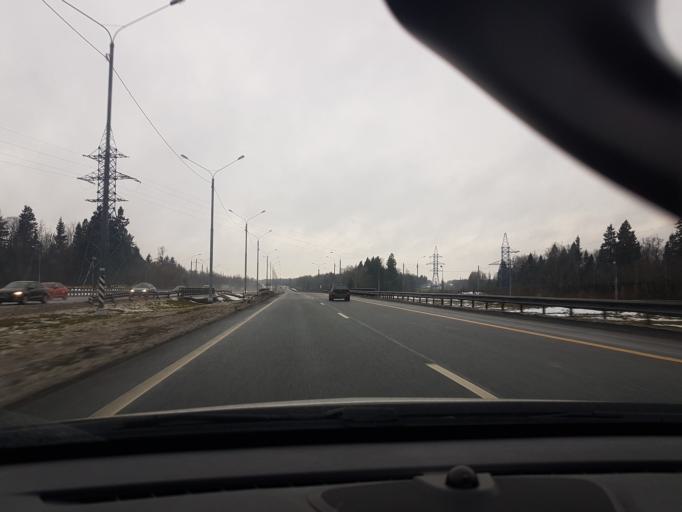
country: RU
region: Moskovskaya
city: Novopetrovskoye
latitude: 55.9810
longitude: 36.4422
